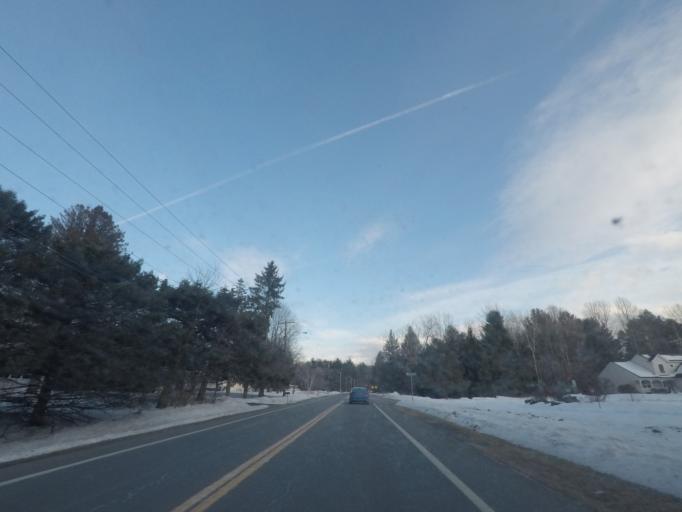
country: US
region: New York
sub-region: Saratoga County
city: Country Knolls
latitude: 42.8403
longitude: -73.7975
